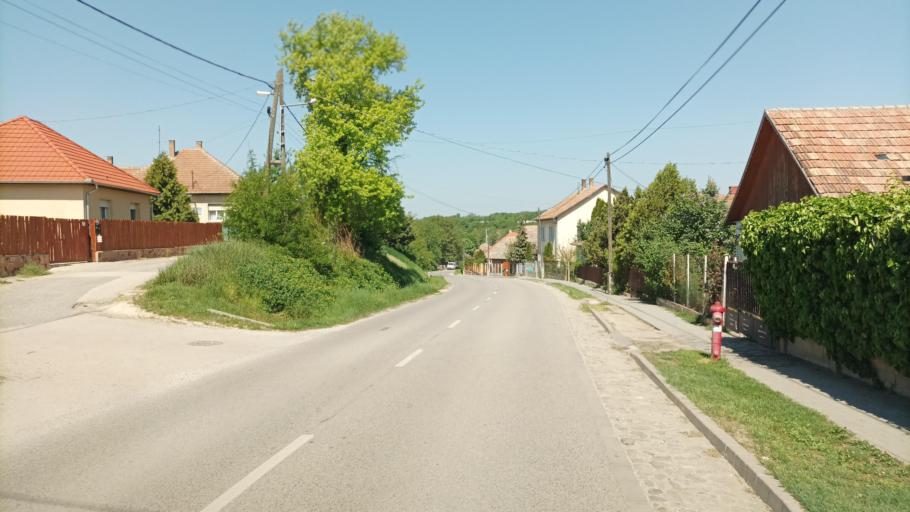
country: HU
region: Pest
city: Uri
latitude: 47.4128
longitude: 19.5216
